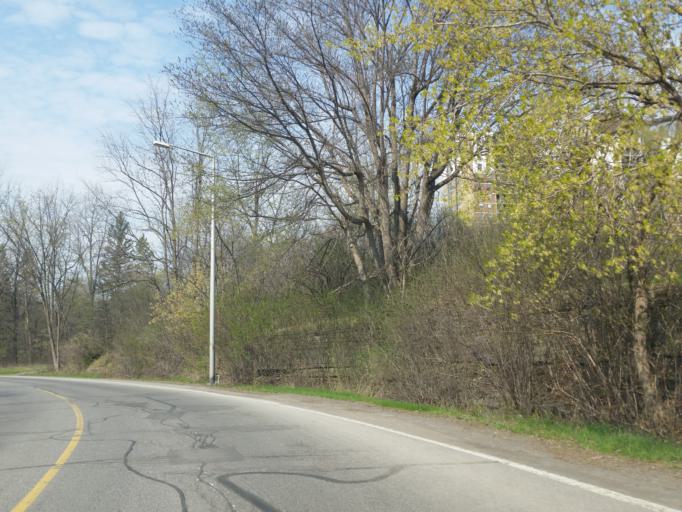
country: CA
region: Ontario
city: Ottawa
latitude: 45.4453
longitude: -75.6201
